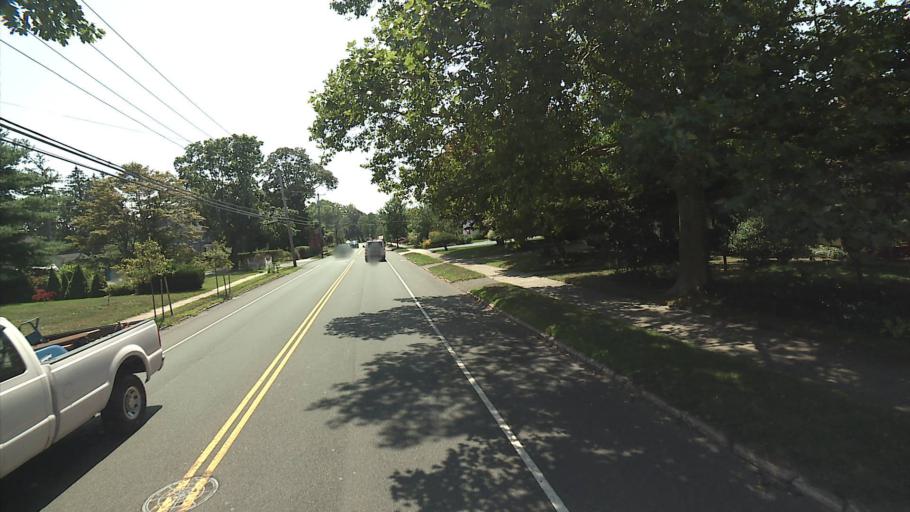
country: US
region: Connecticut
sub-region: New Haven County
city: East Haven
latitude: 41.2740
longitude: -72.8965
